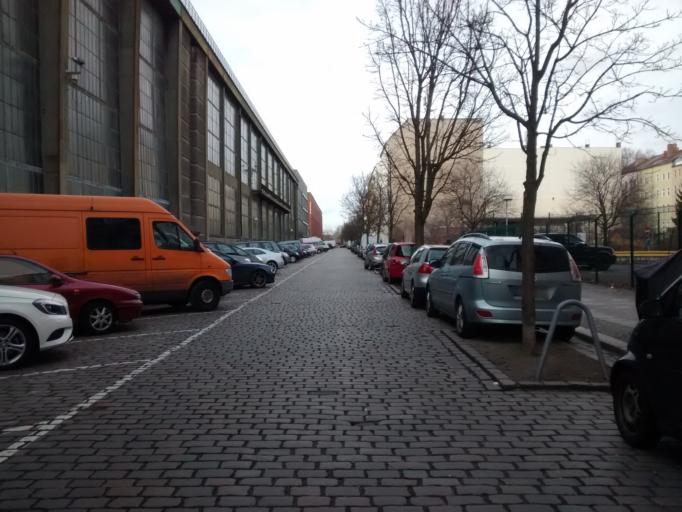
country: DE
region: Berlin
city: Moabit
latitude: 52.5287
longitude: 13.3249
